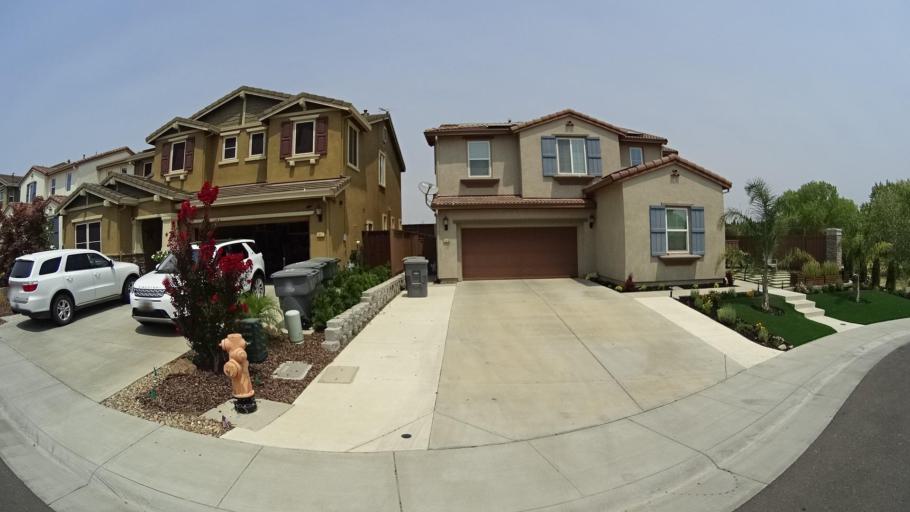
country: US
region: California
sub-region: Placer County
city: Rocklin
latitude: 38.8019
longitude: -121.2817
